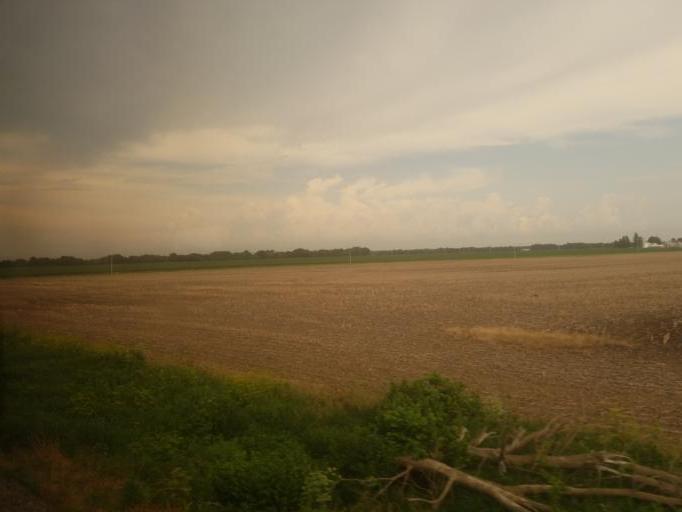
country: US
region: Illinois
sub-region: Bureau County
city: Princeton
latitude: 41.3862
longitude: -89.5231
